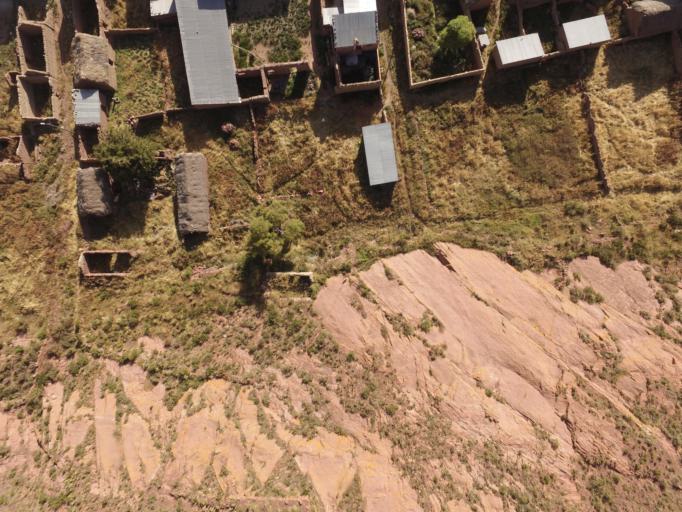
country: BO
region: Oruro
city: Challapata
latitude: -18.6917
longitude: -66.7561
